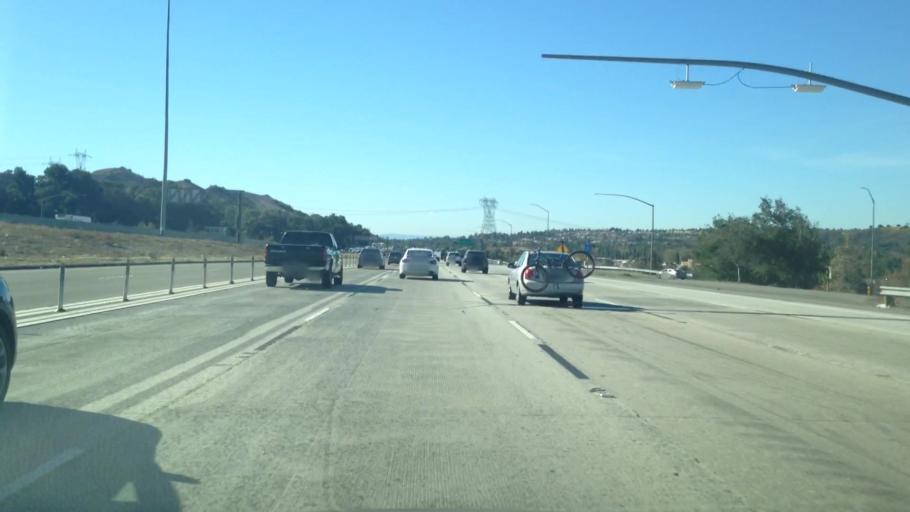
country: US
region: California
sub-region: Orange County
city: Yorba Linda
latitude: 33.8711
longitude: -117.7427
